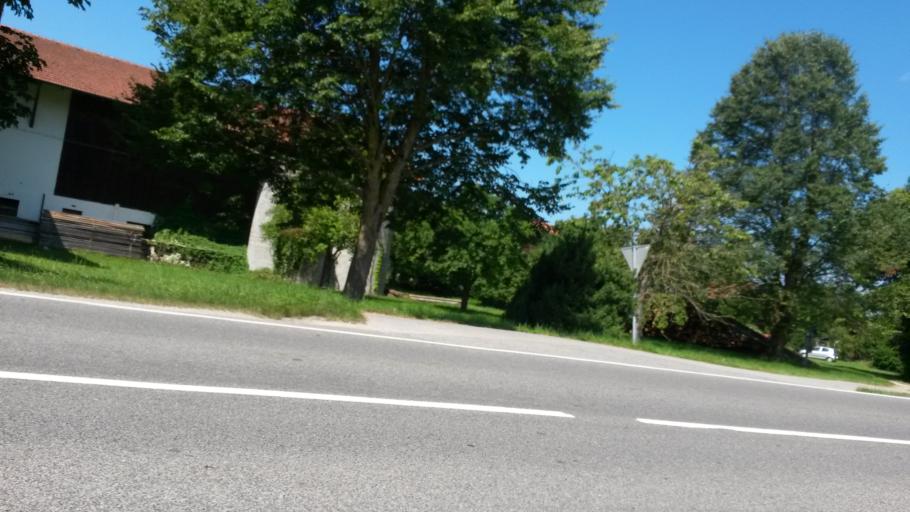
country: DE
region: Bavaria
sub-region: Upper Bavaria
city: Chieming
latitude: 47.8726
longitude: 12.5288
